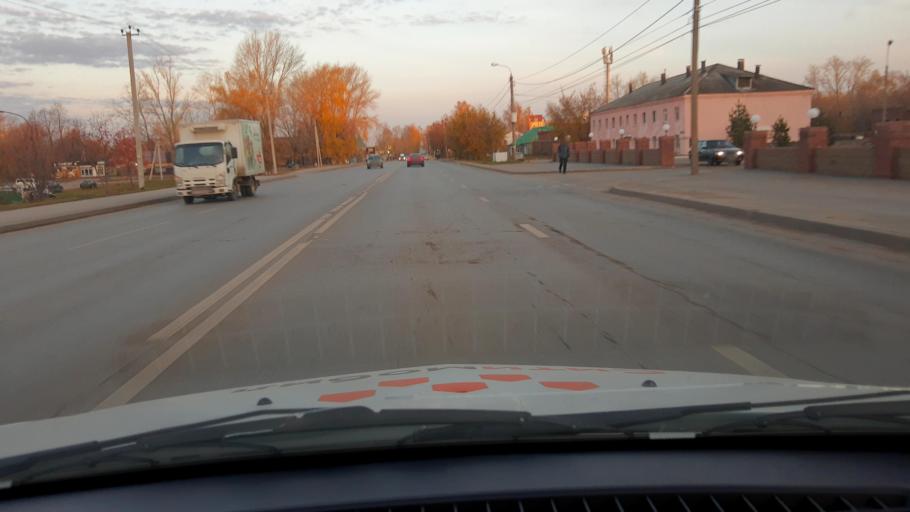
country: RU
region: Bashkortostan
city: Iglino
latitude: 54.7701
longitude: 56.2311
